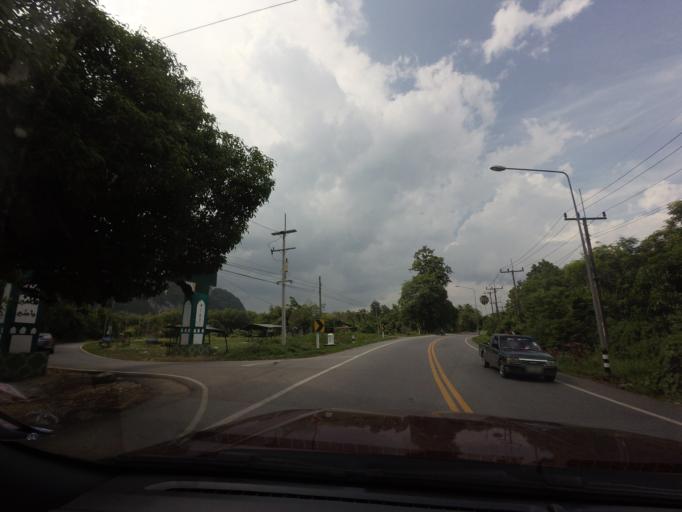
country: TH
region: Yala
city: Ban Nang Sata
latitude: 6.2509
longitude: 101.2219
